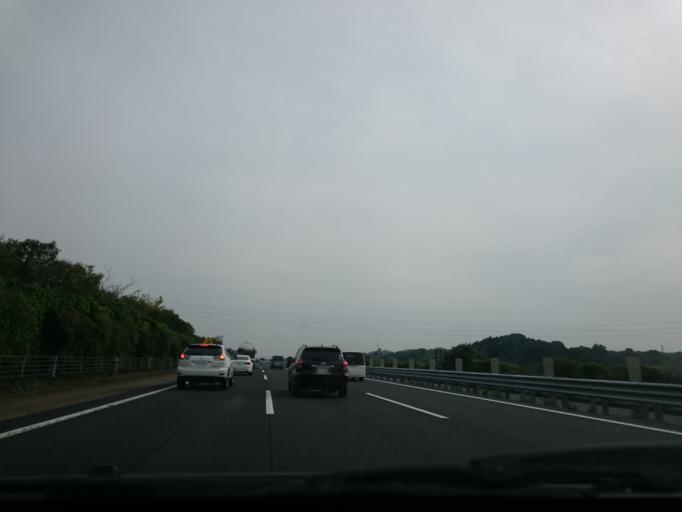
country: JP
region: Tochigi
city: Kanuma
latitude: 36.4877
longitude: 139.7364
